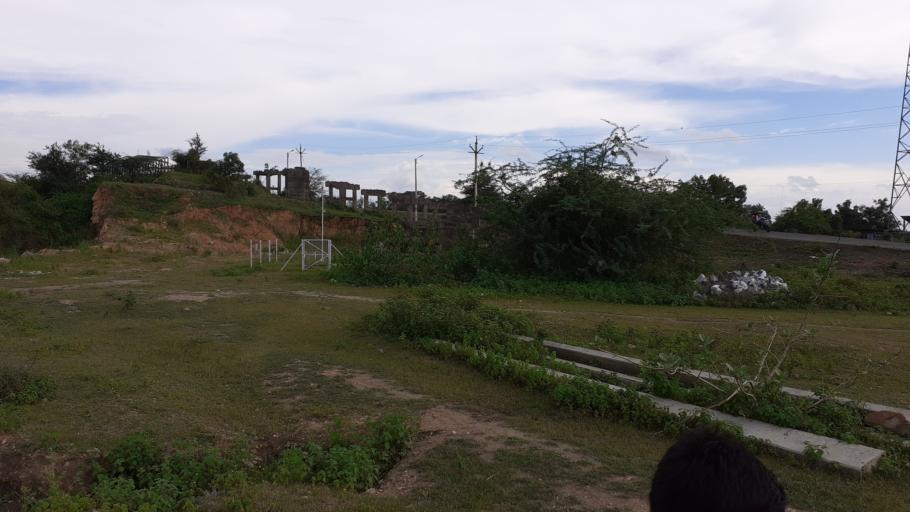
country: IN
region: Maharashtra
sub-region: Nagpur Division
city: Koradih
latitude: 21.2498
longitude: 79.1161
